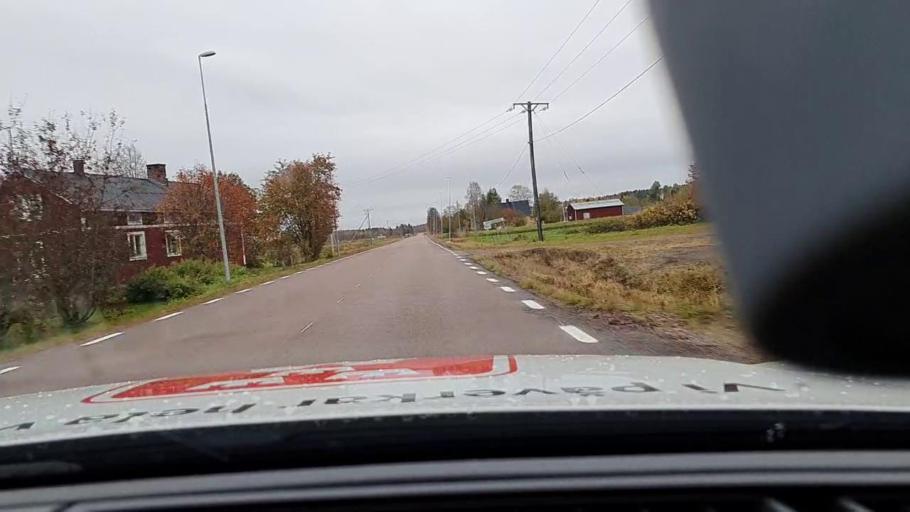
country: FI
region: Lapland
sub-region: Torniolaakso
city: Ylitornio
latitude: 66.1370
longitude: 23.9028
